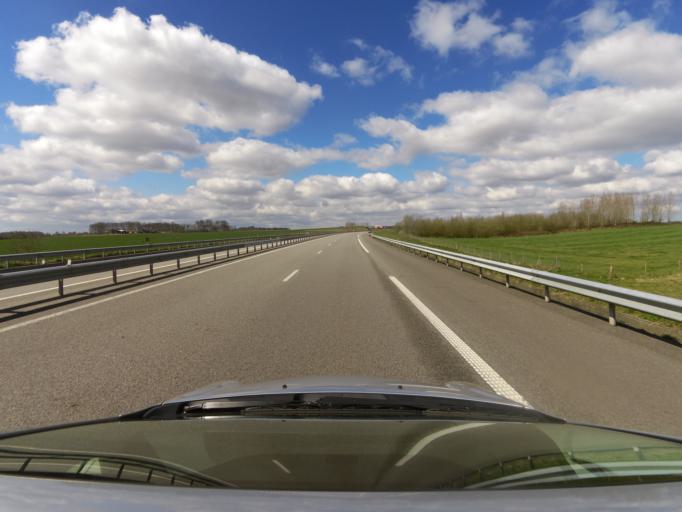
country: FR
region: Haute-Normandie
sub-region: Departement de la Seine-Maritime
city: Limesy
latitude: 49.6463
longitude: 0.9637
